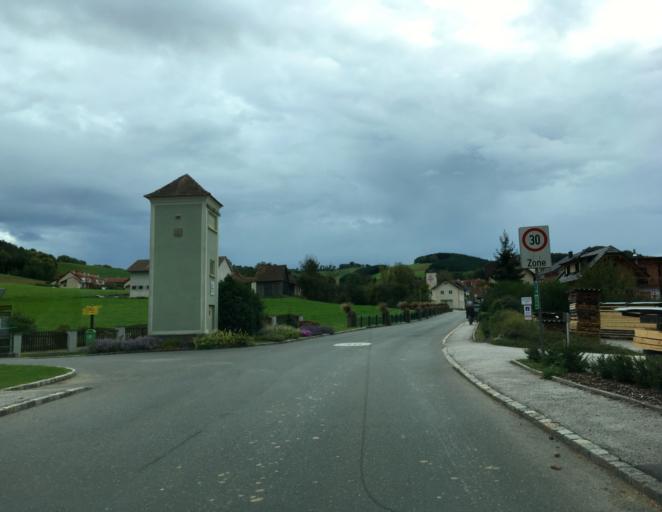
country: AT
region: Lower Austria
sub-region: Politischer Bezirk Wiener Neustadt
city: Bad Schonau
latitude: 47.4987
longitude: 16.2332
